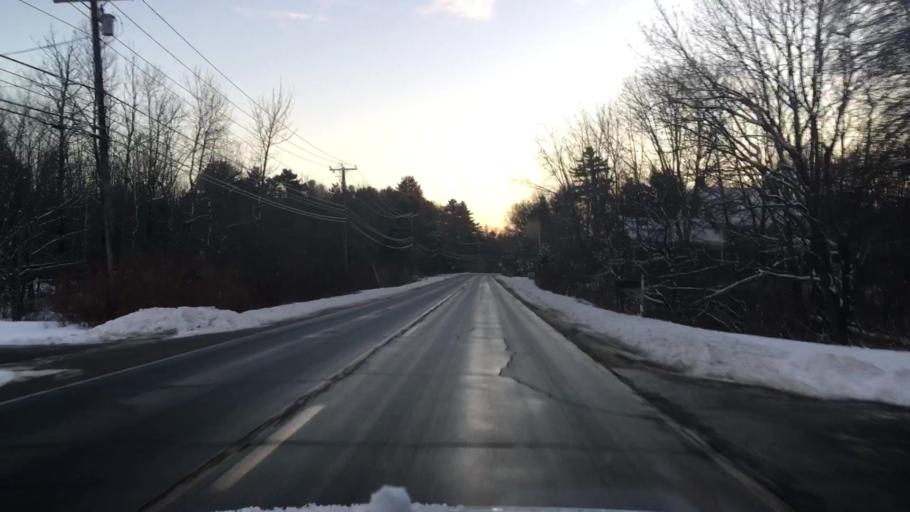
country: US
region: Maine
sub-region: Cumberland County
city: Brunswick
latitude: 43.9447
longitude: -69.9290
